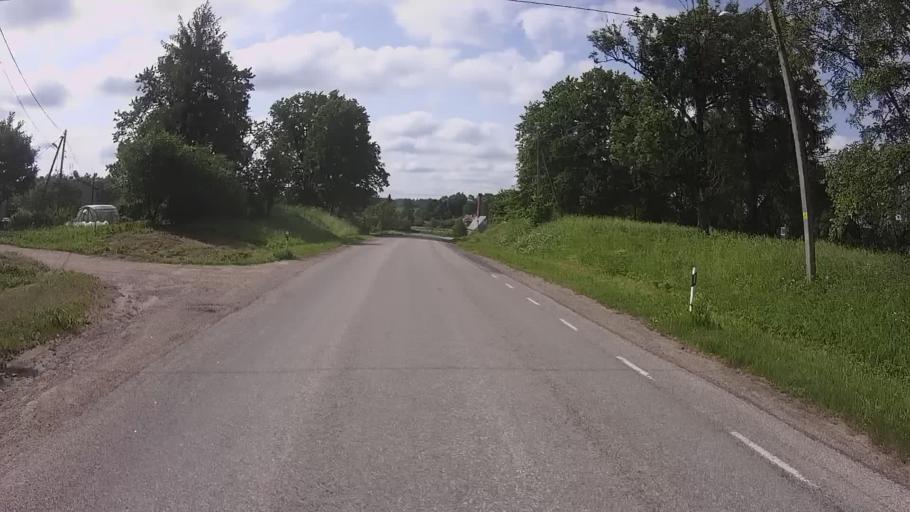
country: EE
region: Vorumaa
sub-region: Antsla vald
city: Vana-Antsla
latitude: 57.8624
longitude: 26.6087
